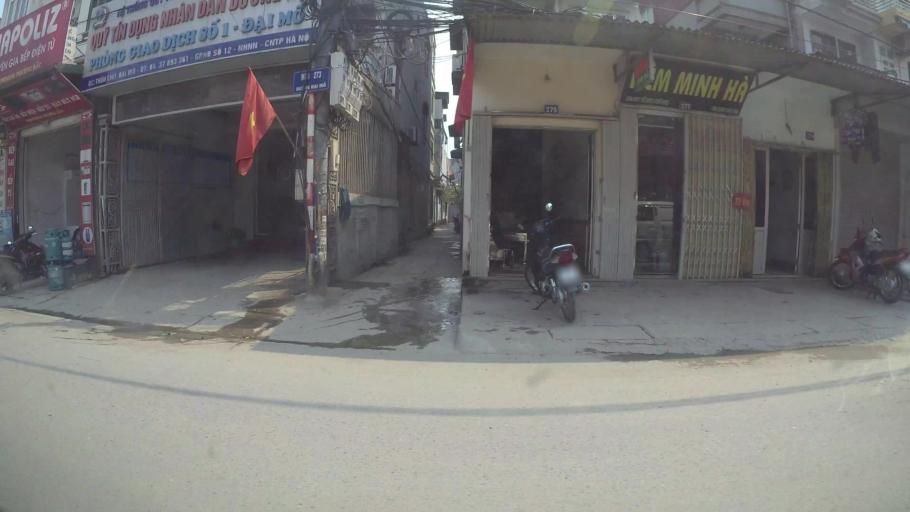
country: VN
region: Ha Noi
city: Ha Dong
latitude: 20.9951
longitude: 105.7587
